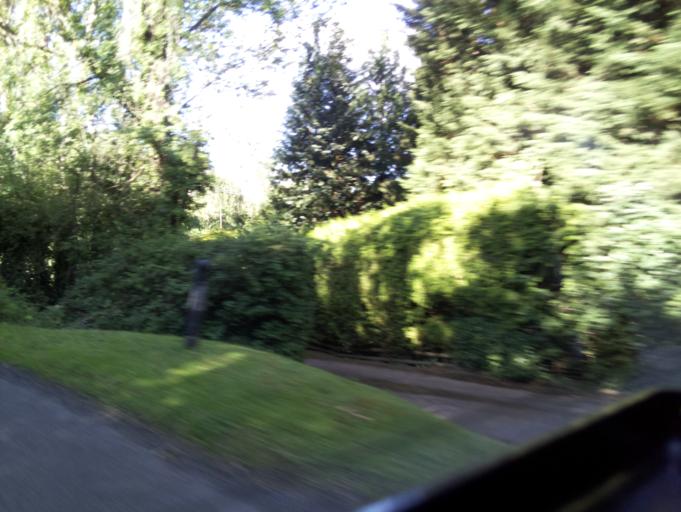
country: GB
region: England
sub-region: Gloucestershire
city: Lydbrook
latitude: 51.8538
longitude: -2.5987
